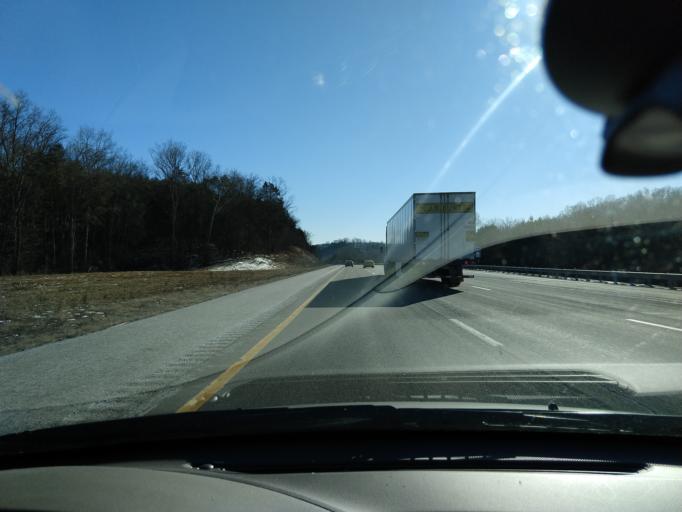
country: US
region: Virginia
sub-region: Rockbridge County
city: East Lexington
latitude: 37.7878
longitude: -79.4001
